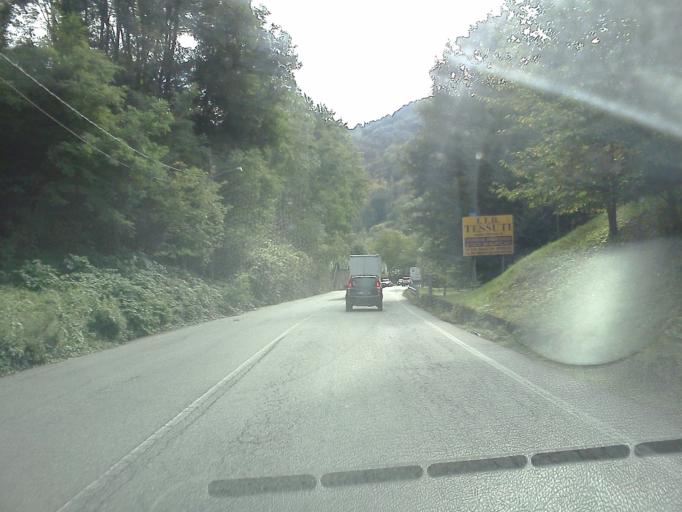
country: IT
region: Piedmont
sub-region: Provincia di Biella
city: Valle Mosso
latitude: 45.6310
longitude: 8.1506
